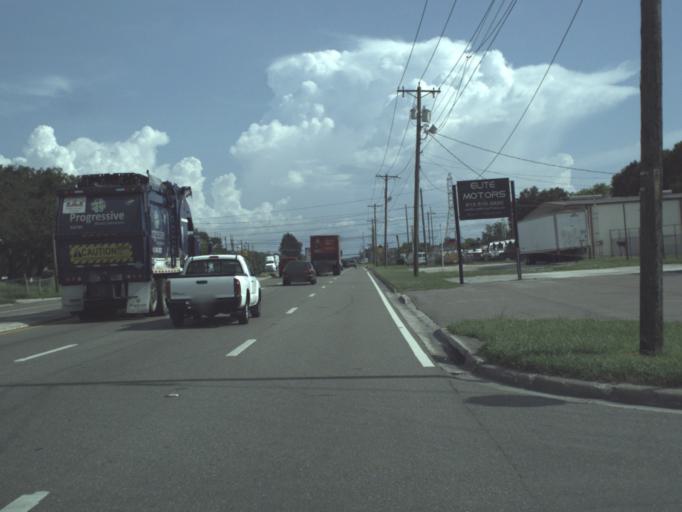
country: US
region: Florida
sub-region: Hillsborough County
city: Palm River-Clair Mel
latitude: 27.9118
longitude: -82.4020
